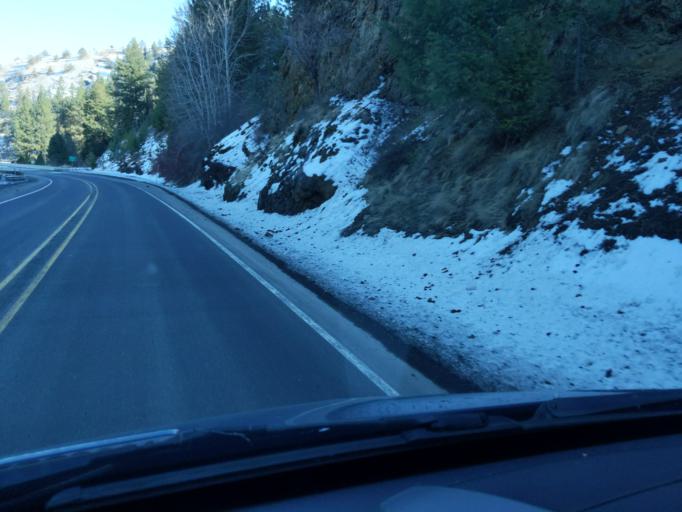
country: US
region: Oregon
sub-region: Grant County
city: John Day
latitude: 44.8358
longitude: -119.0348
